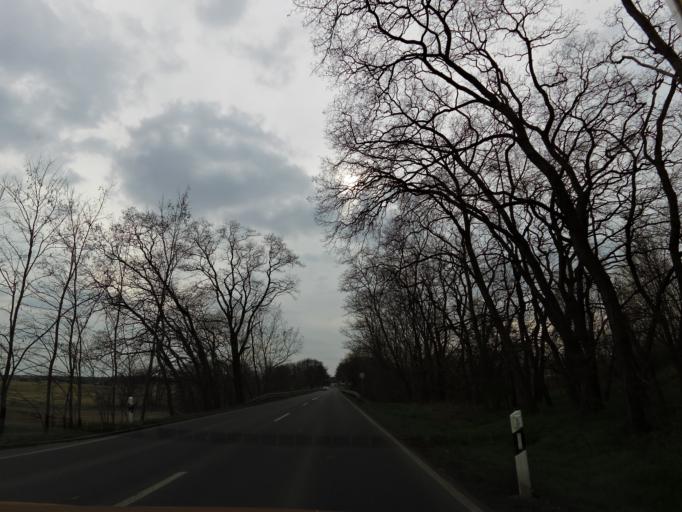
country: DE
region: Brandenburg
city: Frankfurt (Oder)
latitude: 52.3166
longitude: 14.4981
